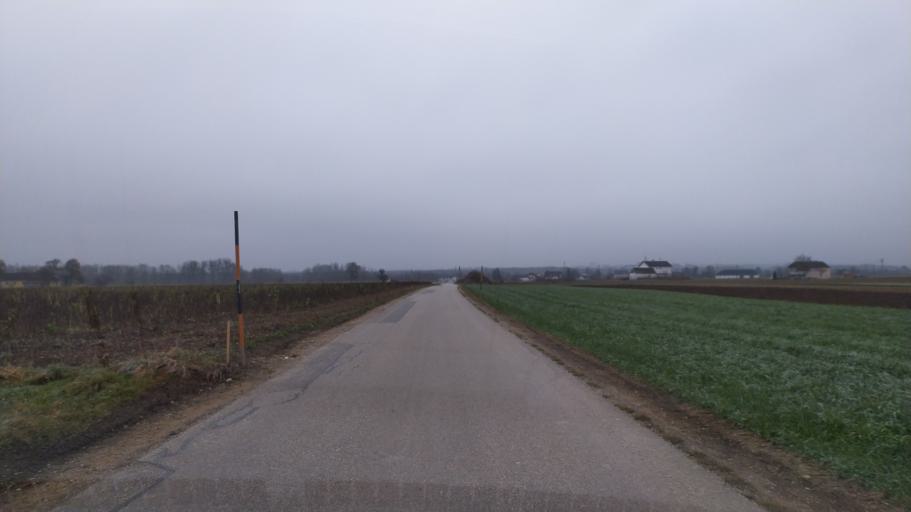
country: AT
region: Upper Austria
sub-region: Politischer Bezirk Perg
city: Perg
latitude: 48.1974
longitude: 14.7196
